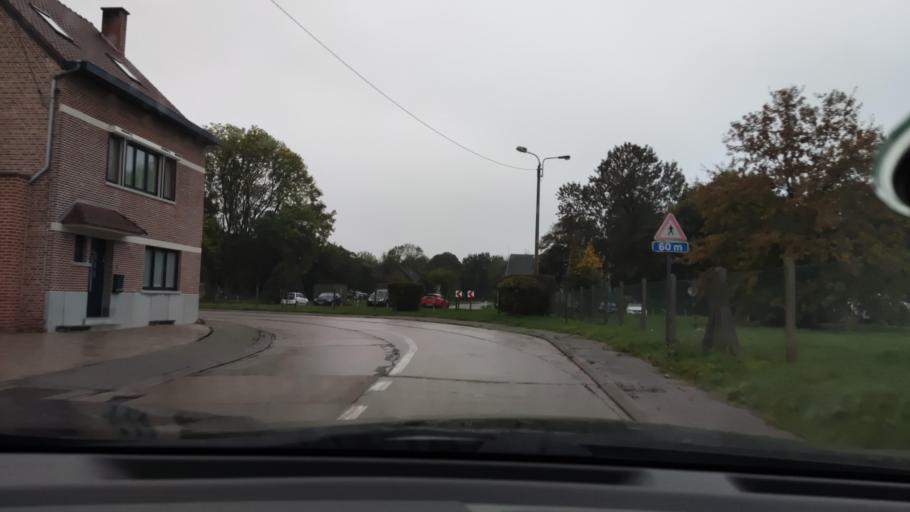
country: BE
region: Wallonia
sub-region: Province du Brabant Wallon
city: Beauvechain
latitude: 50.7573
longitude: 4.7806
